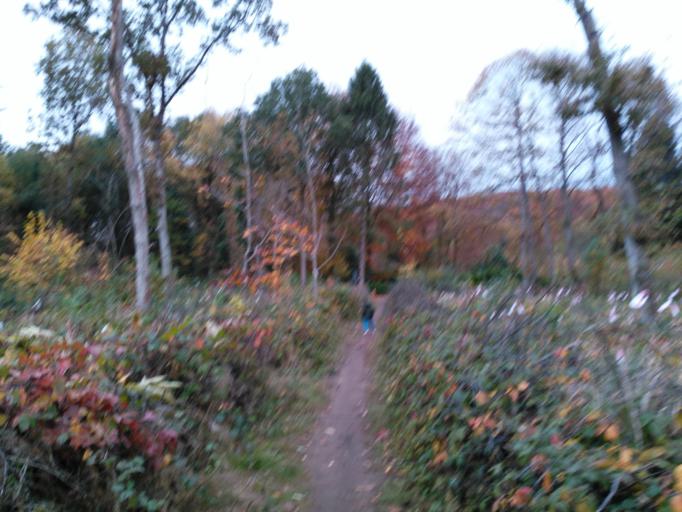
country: BE
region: Flanders
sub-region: Provincie Vlaams-Brabant
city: Holsbeek
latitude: 50.9068
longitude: 4.7348
